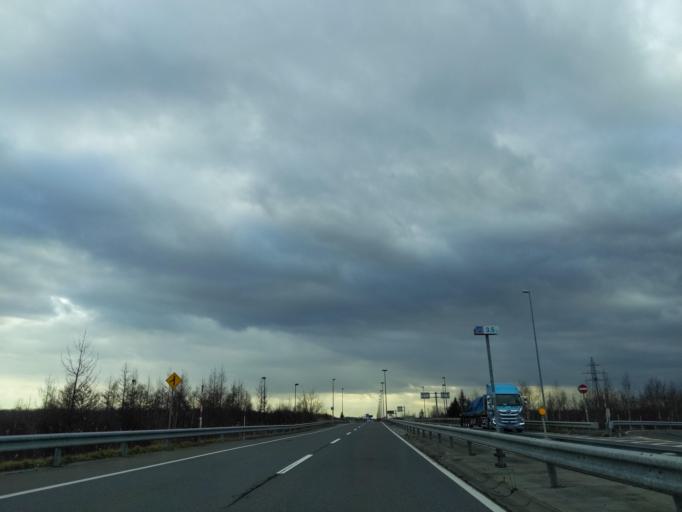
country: JP
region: Hokkaido
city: Chitose
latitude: 42.8272
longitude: 141.6889
